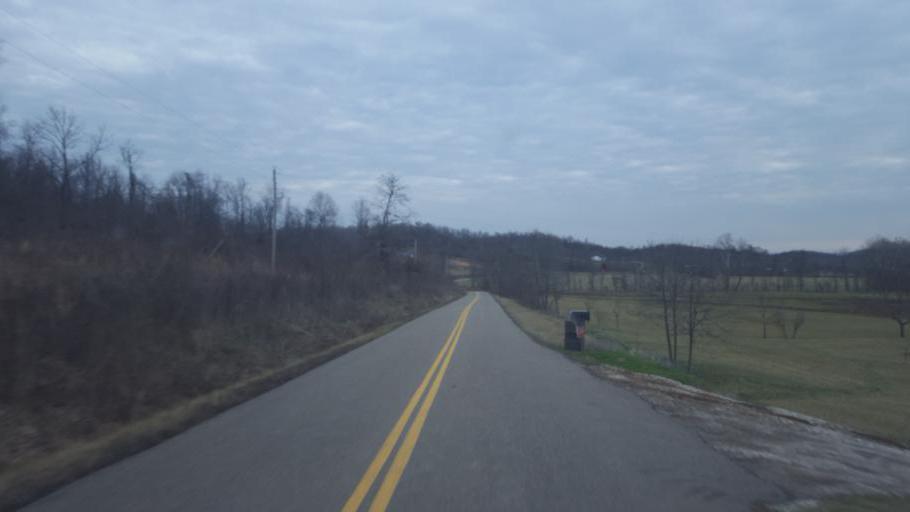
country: US
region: Ohio
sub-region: Gallia County
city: Gallipolis
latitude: 38.7248
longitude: -82.3233
